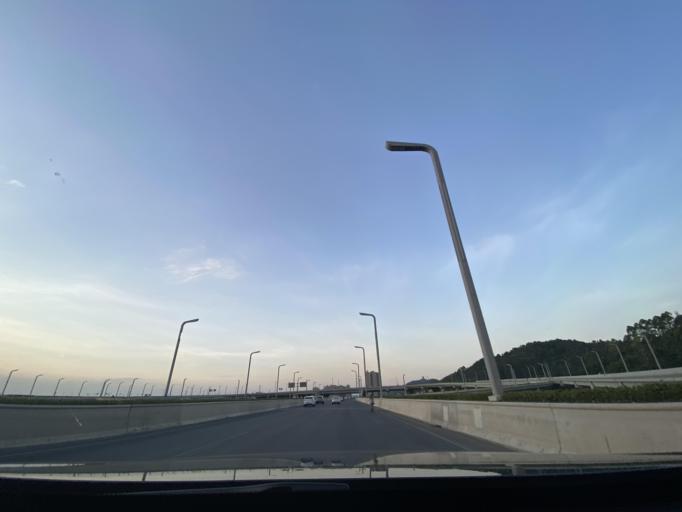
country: CN
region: Sichuan
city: Longquan
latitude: 30.5908
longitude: 104.3033
